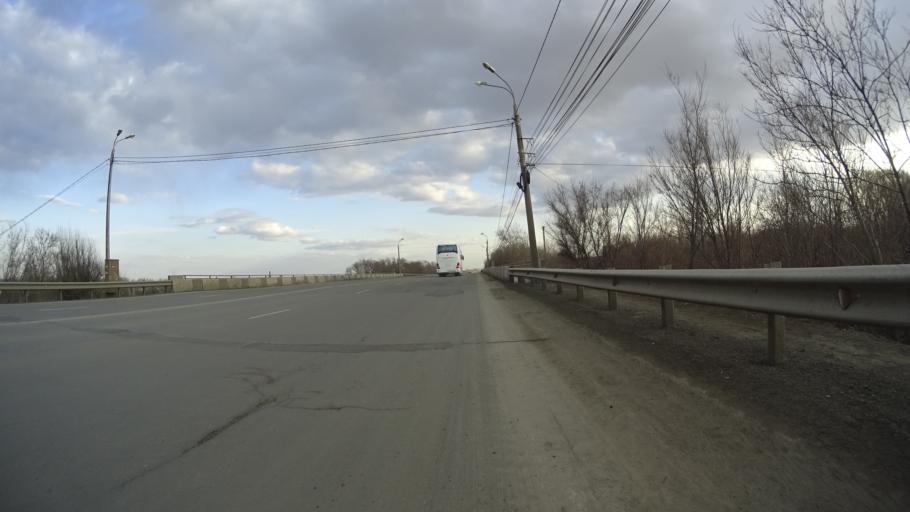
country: RU
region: Chelyabinsk
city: Novosineglazovskiy
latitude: 55.1026
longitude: 61.3875
